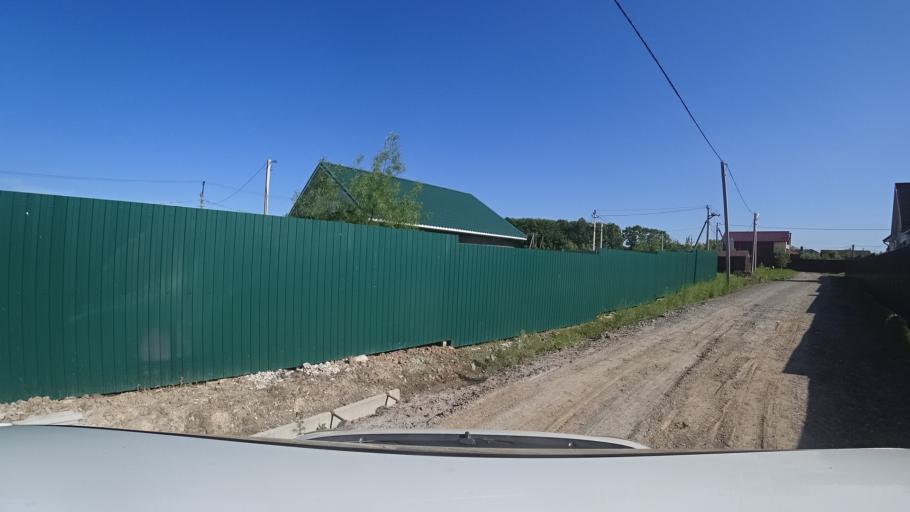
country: RU
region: Khabarovsk Krai
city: Topolevo
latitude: 48.5498
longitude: 135.1825
